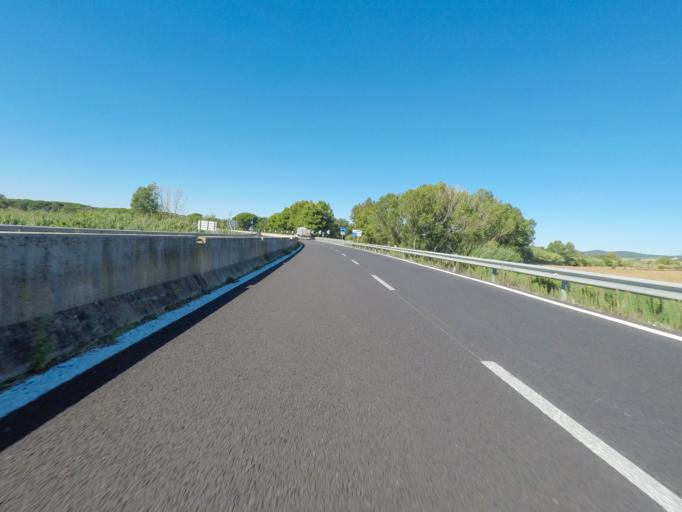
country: IT
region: Latium
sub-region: Provincia di Viterbo
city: Pescia Romana
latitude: 42.4117
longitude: 11.4765
